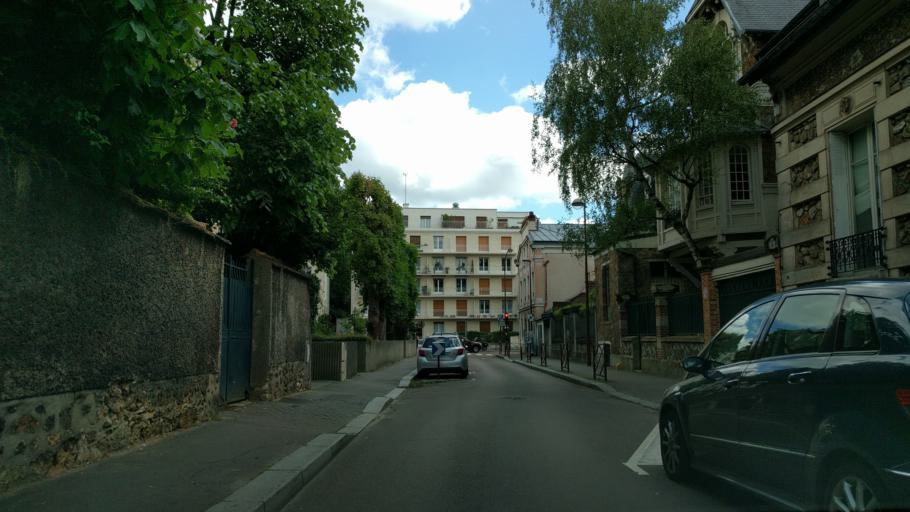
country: FR
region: Ile-de-France
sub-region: Departement des Yvelines
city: Versailles
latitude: 48.8141
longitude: 2.1351
